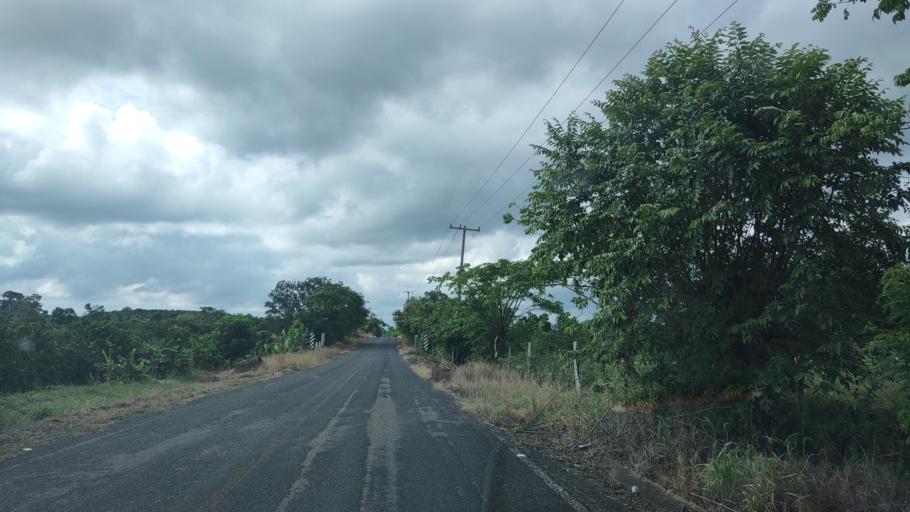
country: MX
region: Veracruz
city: Gutierrez Zamora
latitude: 20.2998
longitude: -97.1342
